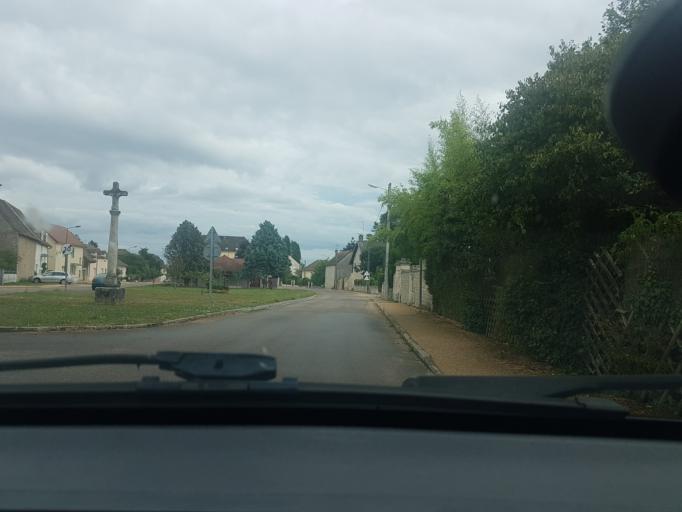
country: FR
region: Bourgogne
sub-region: Departement de Saone-et-Loire
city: Fontaines
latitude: 46.8529
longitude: 4.7676
